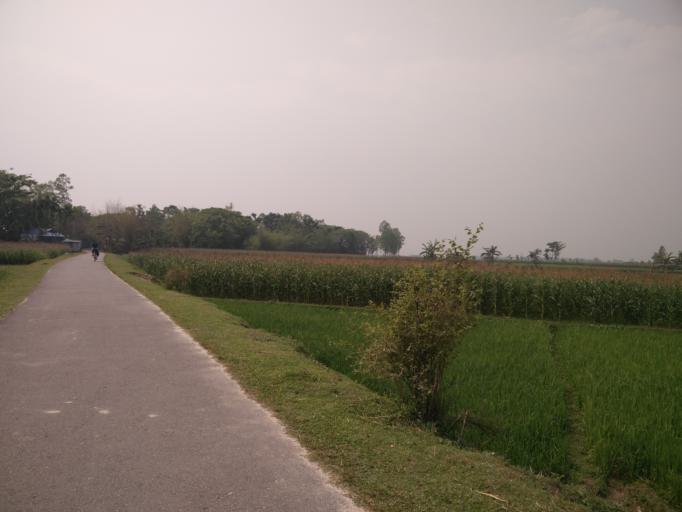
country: BD
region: Dhaka
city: Muktagacha
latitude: 24.9013
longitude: 90.2589
